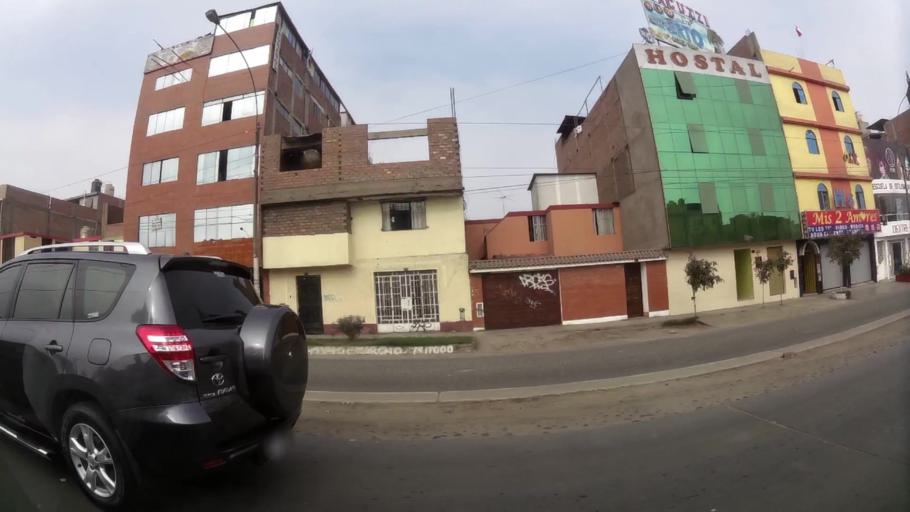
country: PE
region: Callao
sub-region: Callao
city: Callao
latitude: -12.0350
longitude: -77.0966
